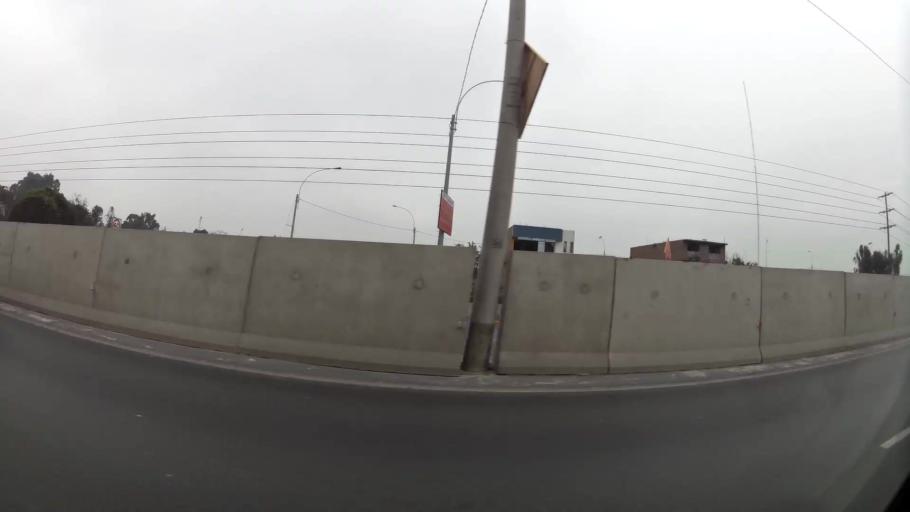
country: PE
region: Lima
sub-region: Lima
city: Urb. Santo Domingo
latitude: -11.9166
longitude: -77.0738
